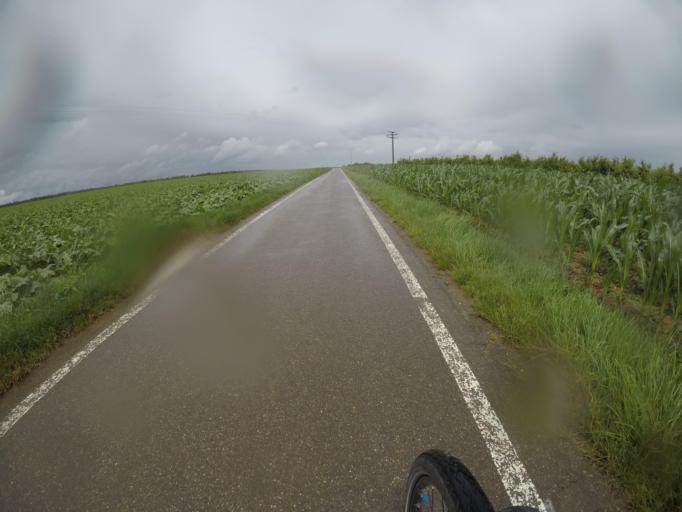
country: DE
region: Baden-Wuerttemberg
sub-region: Regierungsbezirk Stuttgart
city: Bondorf
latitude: 48.5320
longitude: 8.8220
